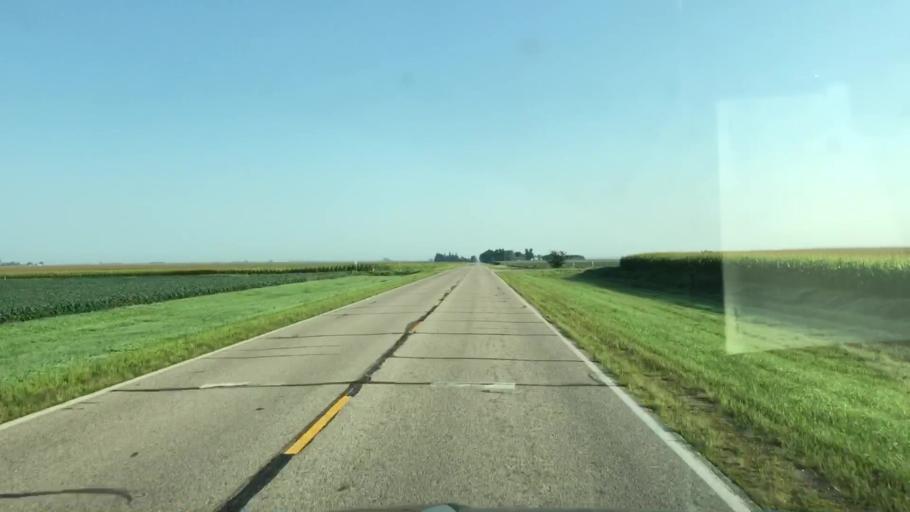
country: US
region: Iowa
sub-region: Lyon County
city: George
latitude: 43.4170
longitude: -95.9982
